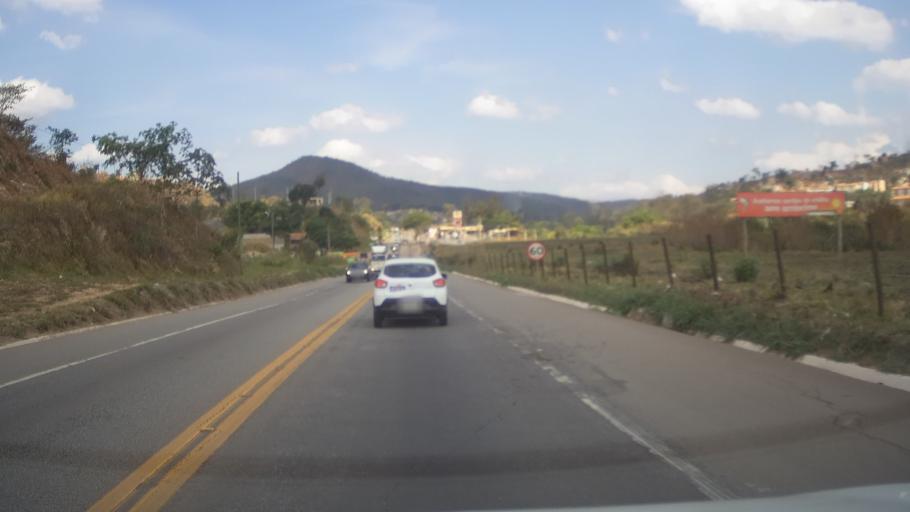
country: BR
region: Minas Gerais
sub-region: Santa Luzia
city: Santa Luzia
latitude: -19.8390
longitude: -43.8803
